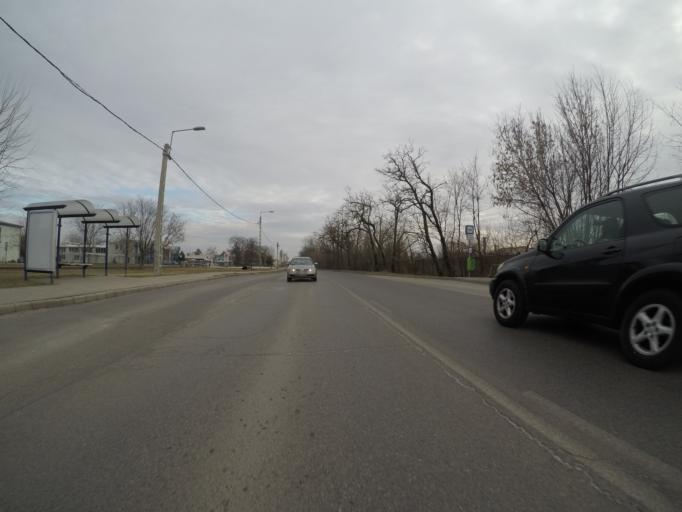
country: HU
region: Budapest
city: Budapest X. keruelet
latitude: 47.4957
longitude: 19.1605
